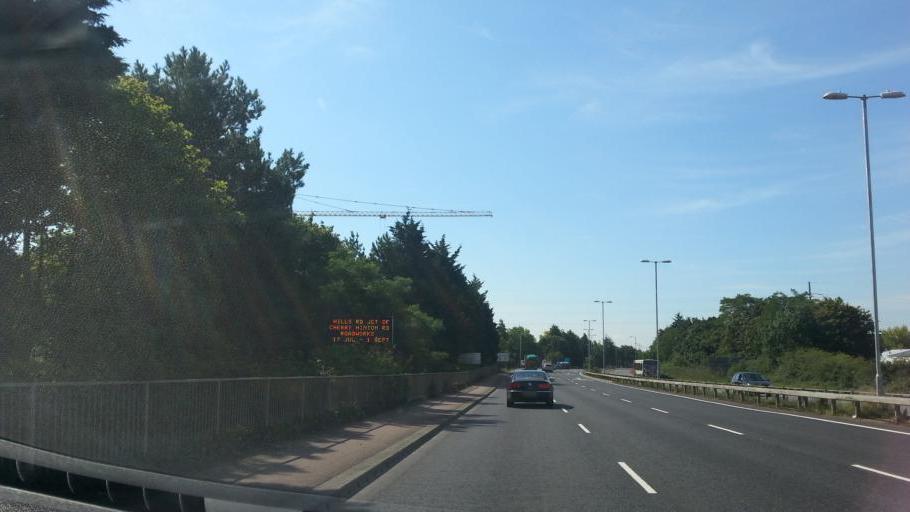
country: GB
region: England
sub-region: Cambridgeshire
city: Histon
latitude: 52.2351
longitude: 0.1509
